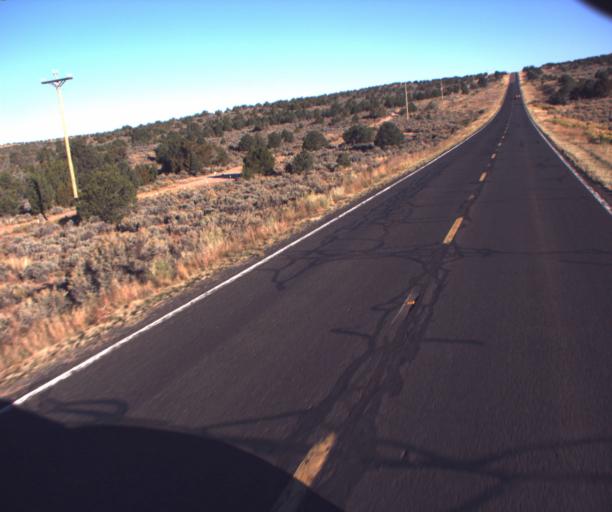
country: US
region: Arizona
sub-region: Apache County
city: Ganado
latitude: 35.6194
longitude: -109.5425
